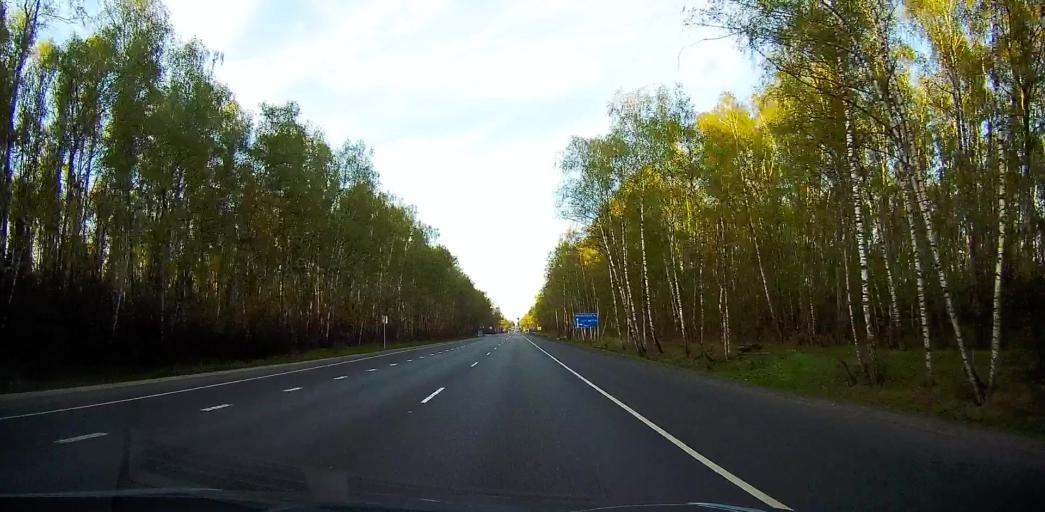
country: RU
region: Moskovskaya
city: Meshcherino
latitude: 55.2315
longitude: 38.4139
